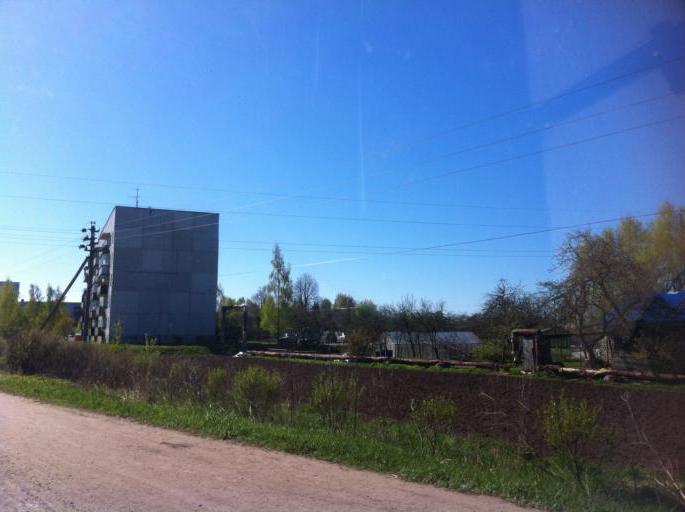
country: RU
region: Pskov
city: Pskov
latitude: 57.7953
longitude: 28.2036
